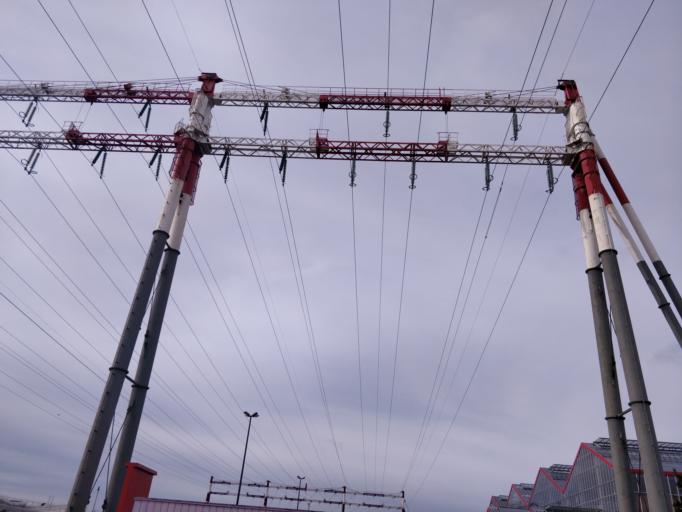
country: FR
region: Ile-de-France
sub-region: Departement du Val-de-Marne
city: Chevilly-Larue
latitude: 48.7672
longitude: 2.3498
